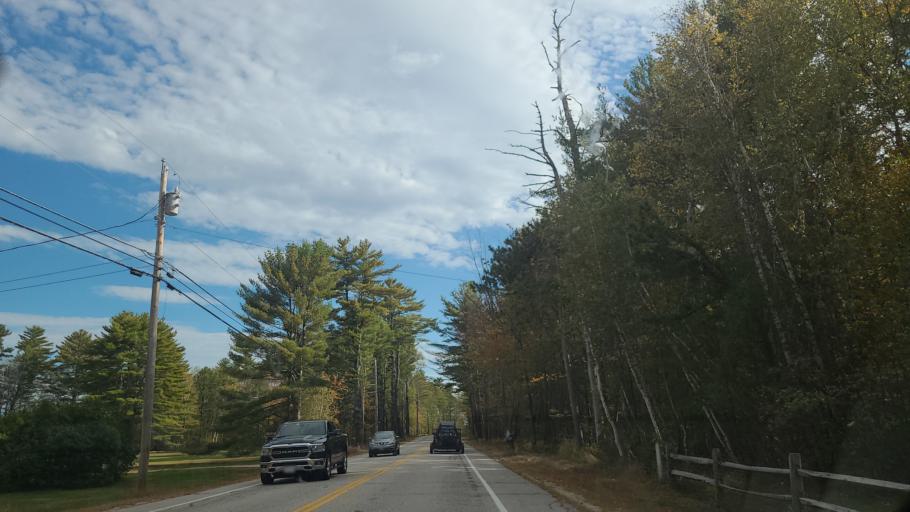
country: US
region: New Hampshire
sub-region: Carroll County
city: North Conway
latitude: 44.0237
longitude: -71.1318
